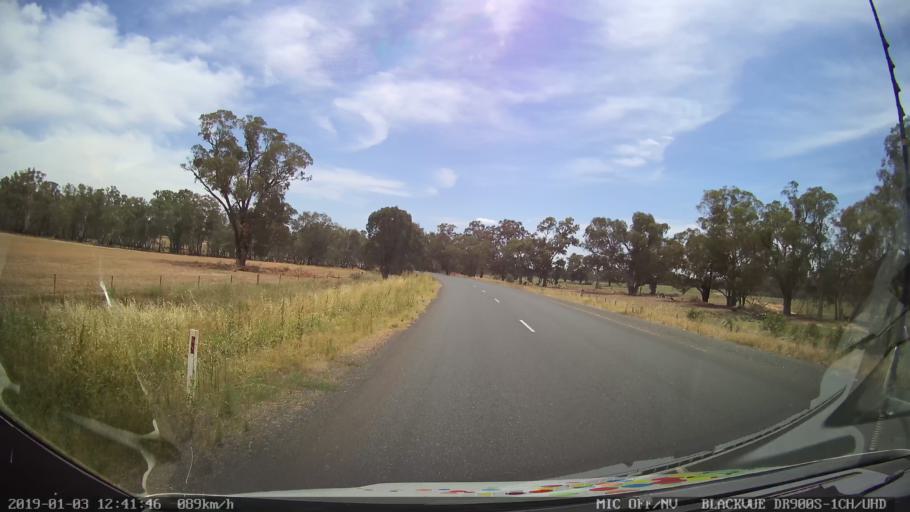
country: AU
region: New South Wales
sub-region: Weddin
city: Grenfell
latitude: -33.7951
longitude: 148.2154
